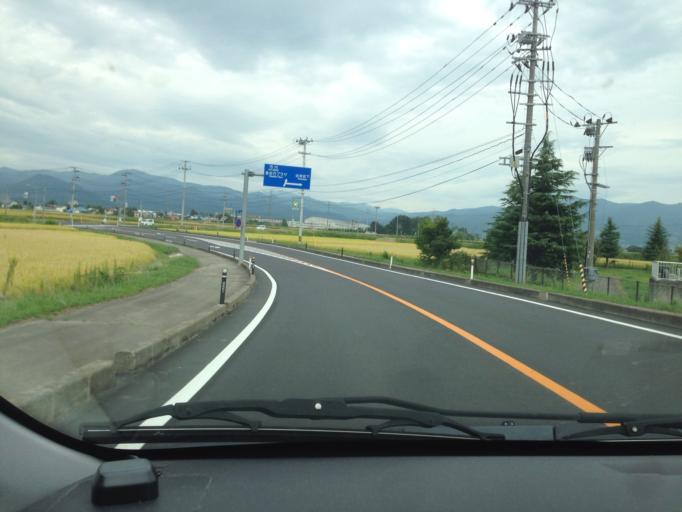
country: JP
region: Fukushima
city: Kitakata
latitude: 37.6370
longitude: 139.8541
